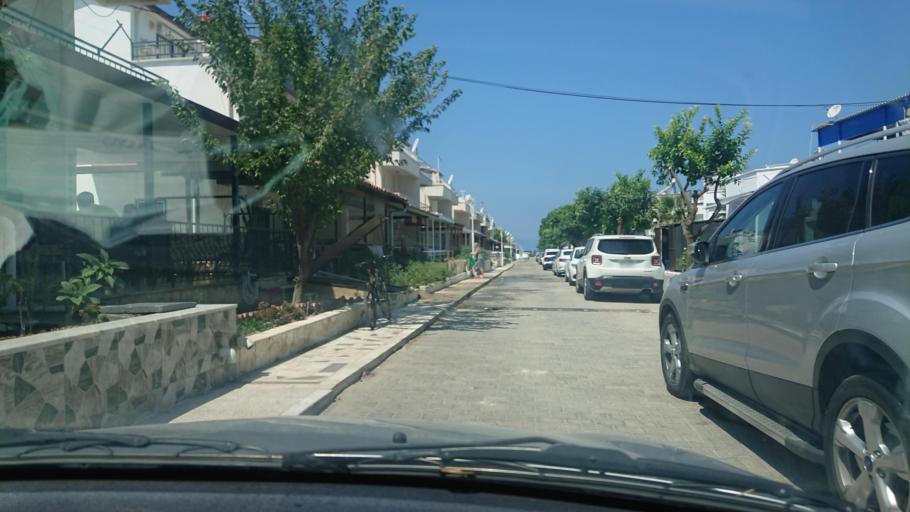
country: TR
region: Aydin
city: Kusadasi
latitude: 37.7986
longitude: 27.2735
